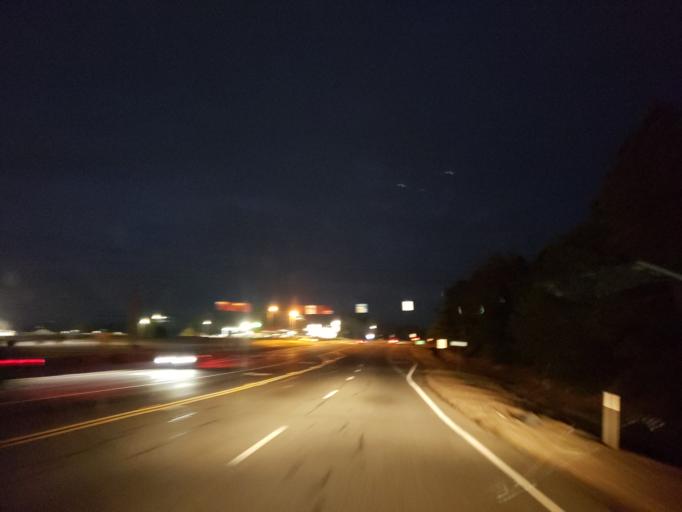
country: US
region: Georgia
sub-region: Polk County
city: Rockmart
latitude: 34.0083
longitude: -85.0286
